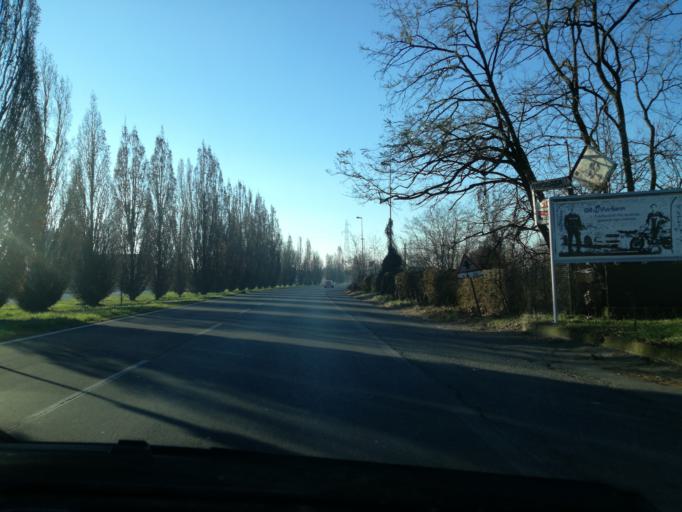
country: IT
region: Lombardy
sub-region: Provincia di Monza e Brianza
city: Brugherio
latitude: 45.5778
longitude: 9.3090
